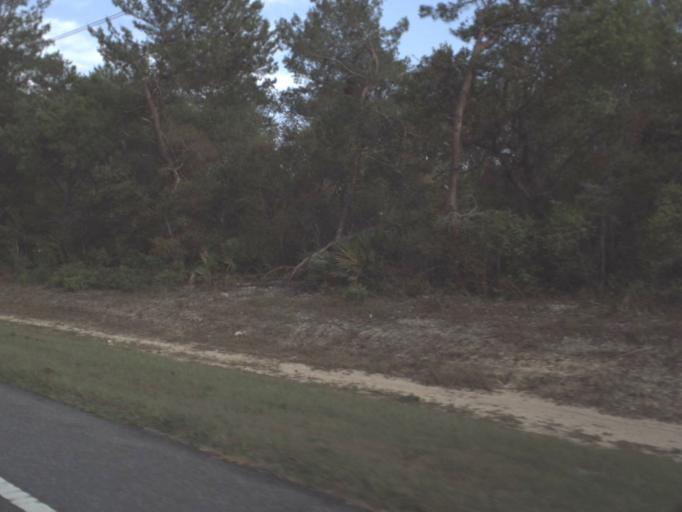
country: US
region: Florida
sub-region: Lake County
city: Astor
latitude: 29.1738
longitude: -81.6899
